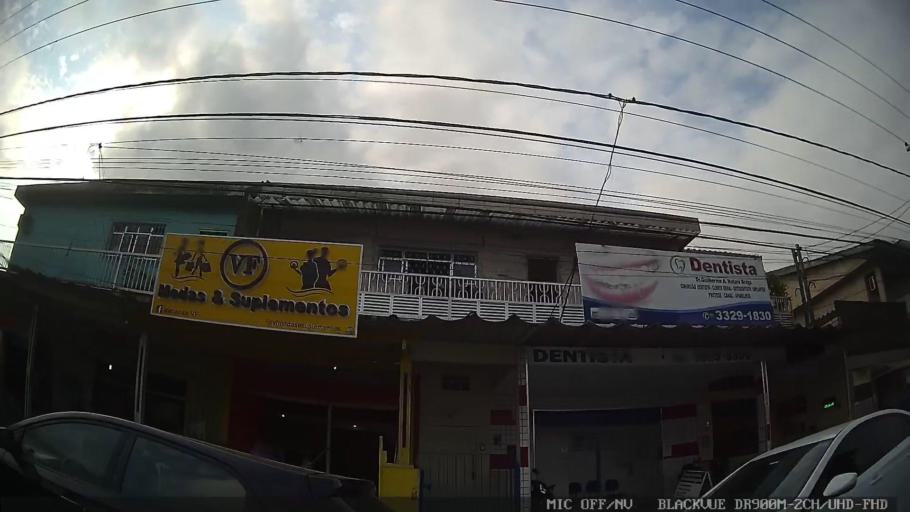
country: BR
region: Sao Paulo
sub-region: Guaruja
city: Guaruja
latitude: -23.9541
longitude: -46.2853
